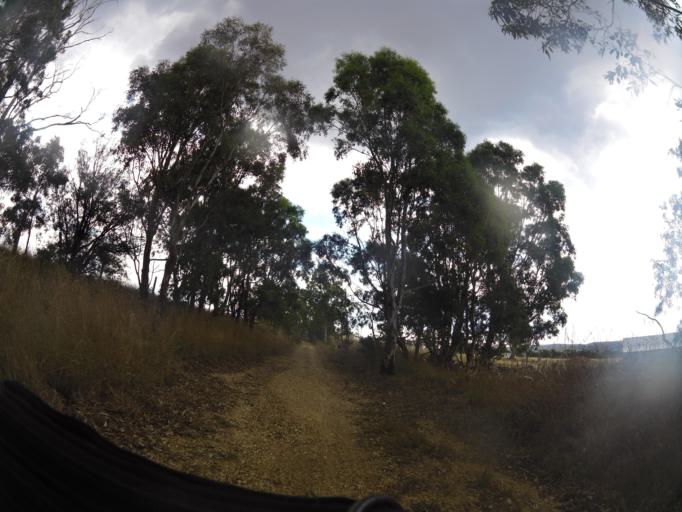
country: AU
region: Victoria
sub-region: Wellington
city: Heyfield
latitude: -38.0237
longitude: 146.6739
